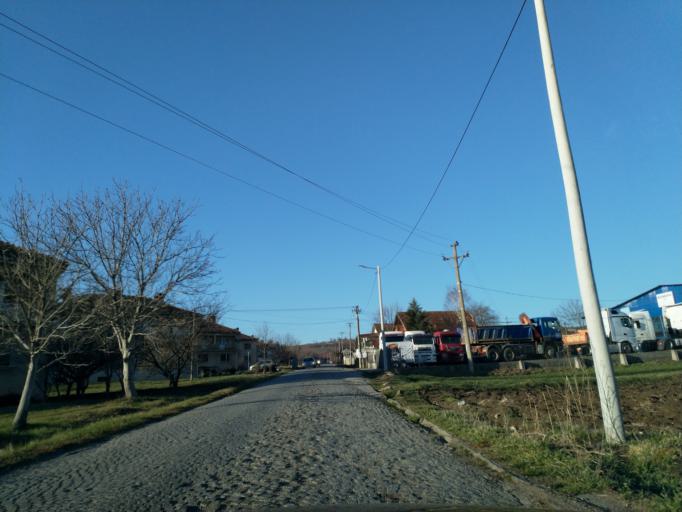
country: RS
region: Central Serbia
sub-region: Pomoravski Okrug
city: Paracin
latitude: 43.9166
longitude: 21.5102
